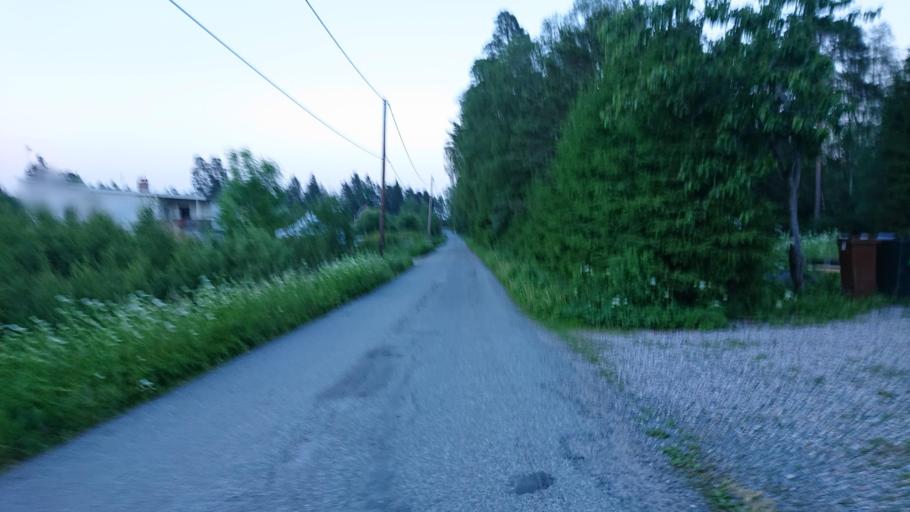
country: SE
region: Stockholm
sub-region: Osterakers Kommun
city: Akersberga
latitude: 59.4725
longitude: 18.2362
